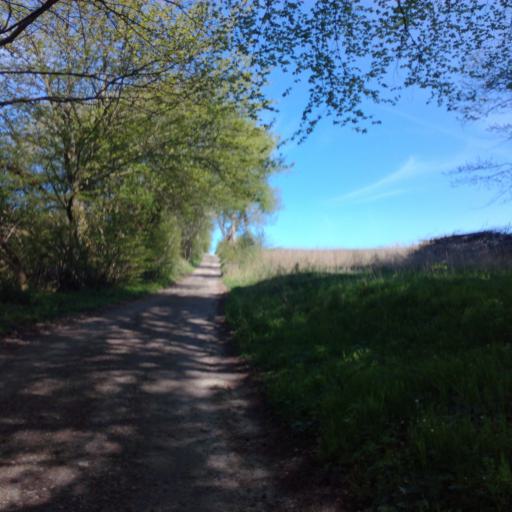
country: DK
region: South Denmark
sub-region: Vejle Kommune
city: Borkop
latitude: 55.6115
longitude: 9.6862
